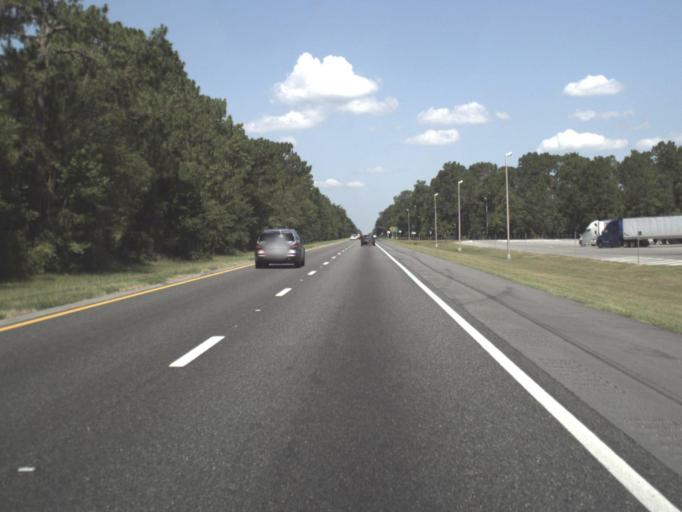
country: US
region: Florida
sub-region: Madison County
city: Madison
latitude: 30.3676
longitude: -83.2427
